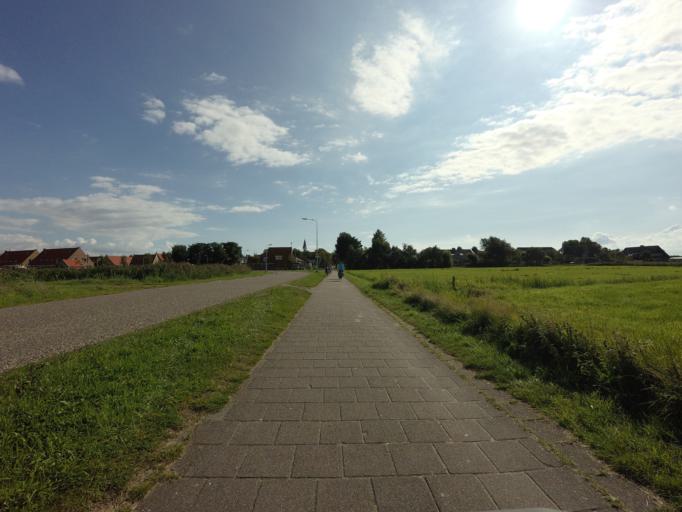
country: NL
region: Friesland
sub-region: Gemeente Terschelling
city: West-Terschelling
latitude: 53.3857
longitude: 5.2847
